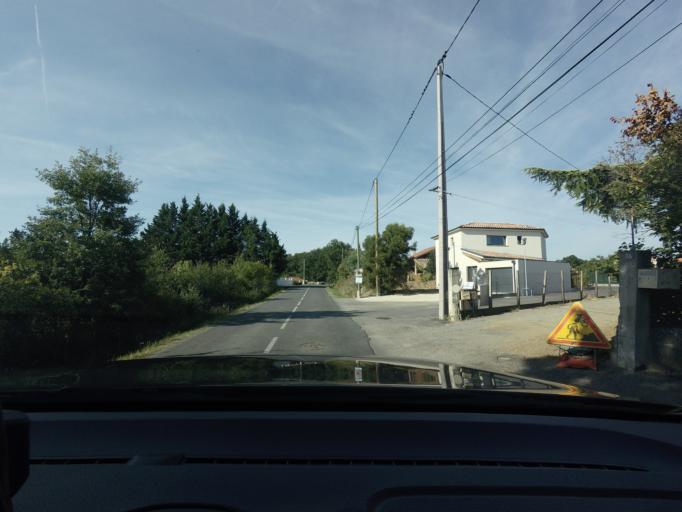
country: FR
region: Midi-Pyrenees
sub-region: Departement de la Haute-Garonne
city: Cornebarrieu
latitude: 43.6414
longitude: 1.3169
